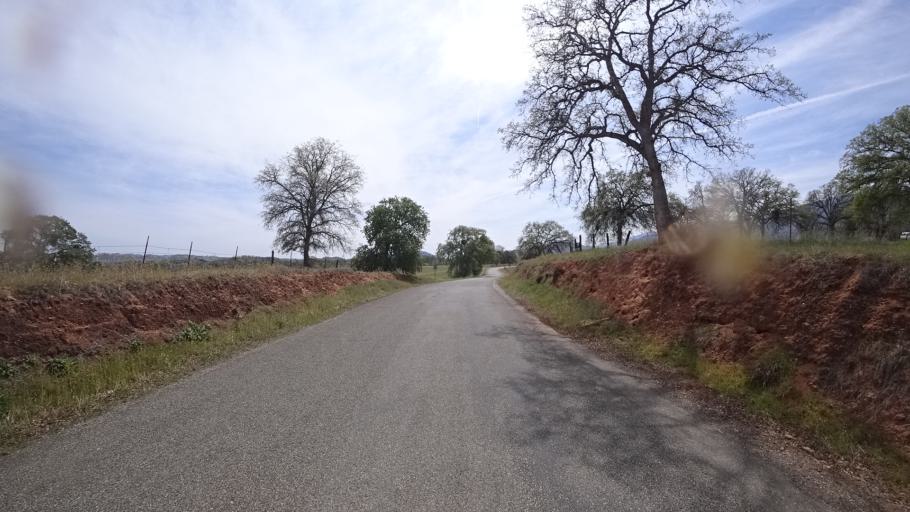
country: US
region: California
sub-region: Glenn County
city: Willows
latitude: 39.5883
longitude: -122.5775
